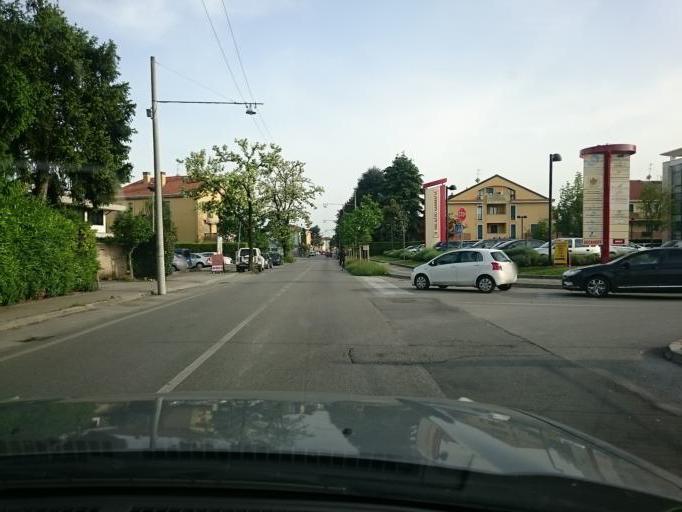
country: IT
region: Veneto
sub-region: Provincia di Padova
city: Noventa
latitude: 45.4030
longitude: 11.9447
